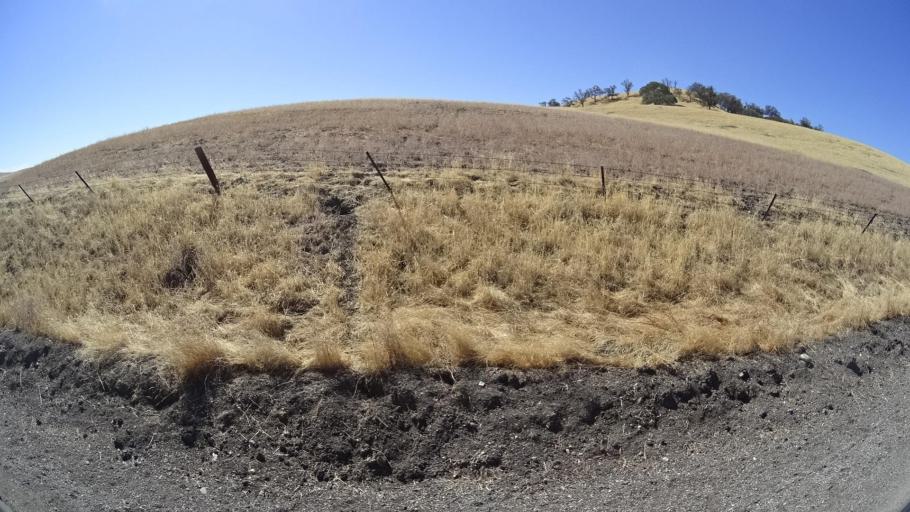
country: US
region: California
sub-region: San Luis Obispo County
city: San Miguel
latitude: 35.8110
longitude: -120.5405
